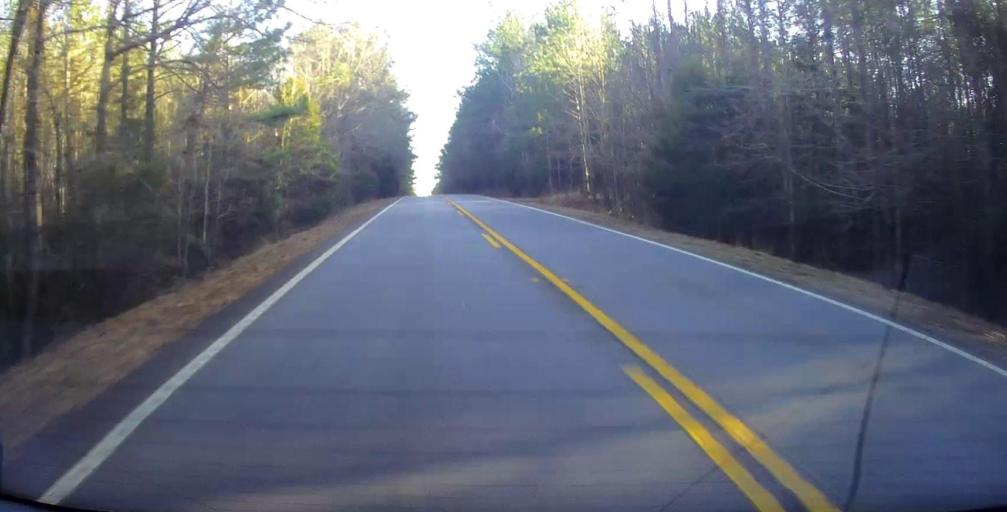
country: US
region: Alabama
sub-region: Chambers County
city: Valley
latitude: 32.8093
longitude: -85.1034
